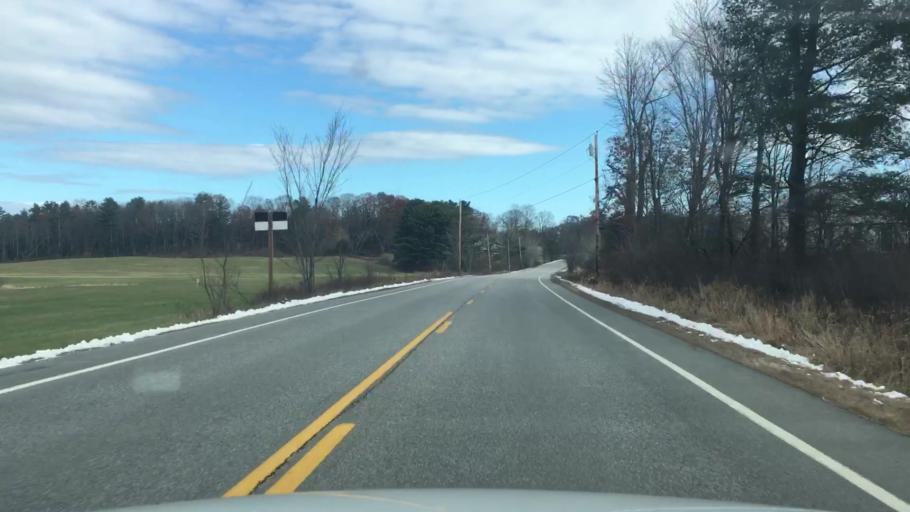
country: US
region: Maine
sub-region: Androscoggin County
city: Leeds
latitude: 44.3440
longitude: -70.1284
